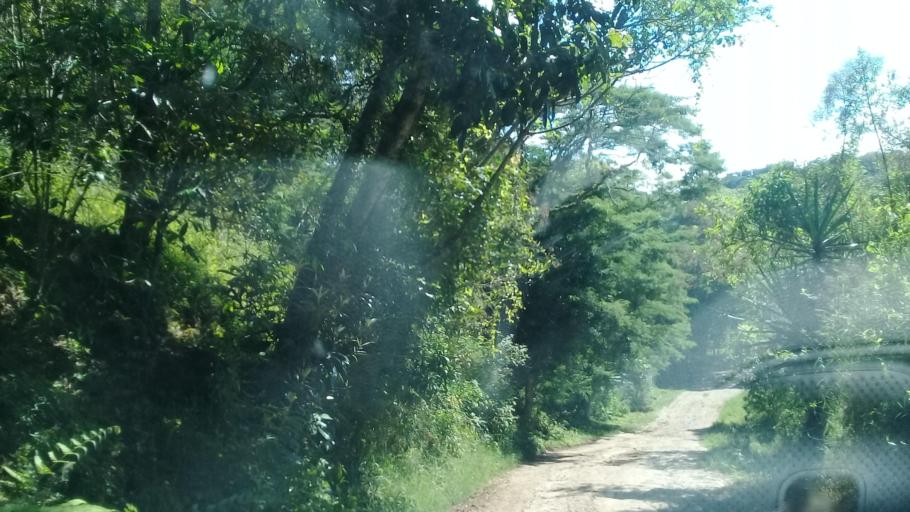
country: MX
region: Veracruz
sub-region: Jilotepec
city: El Pueblito (Garbanzal)
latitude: 19.5790
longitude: -96.9005
